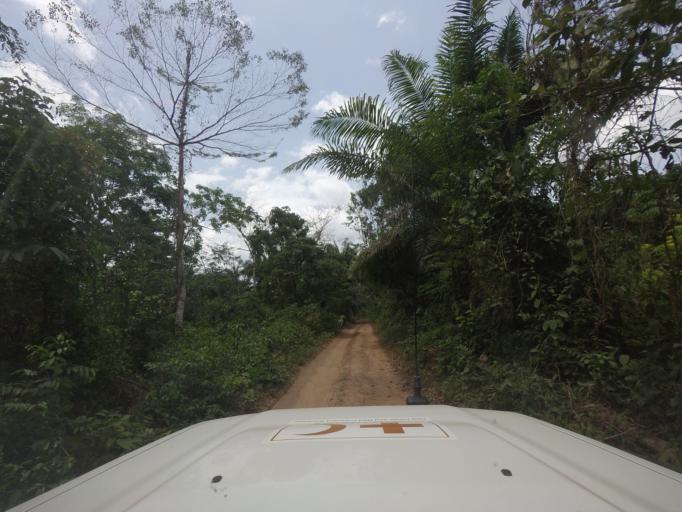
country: LR
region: Bong
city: Gbarnga
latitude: 7.1902
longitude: -9.1996
